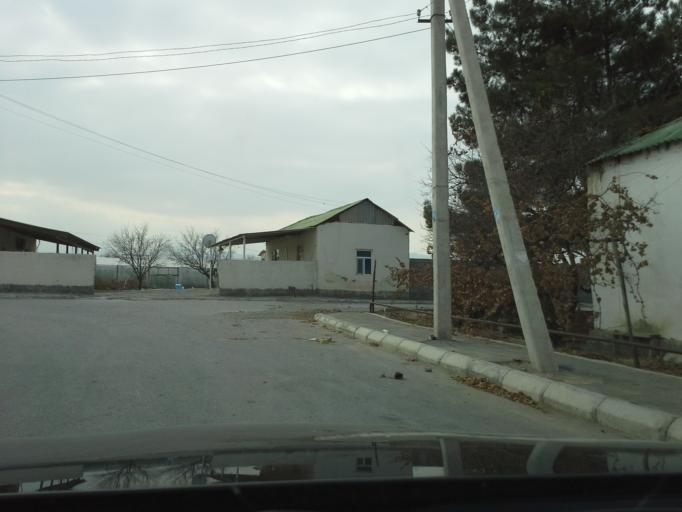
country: TM
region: Ahal
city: Abadan
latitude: 38.0378
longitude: 58.2669
